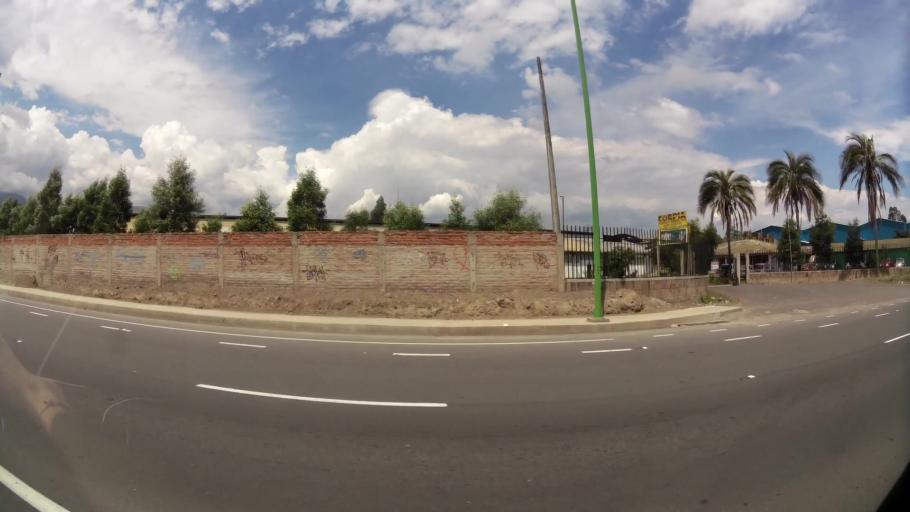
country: EC
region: Pichincha
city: Sangolqui
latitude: -0.2243
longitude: -78.3444
